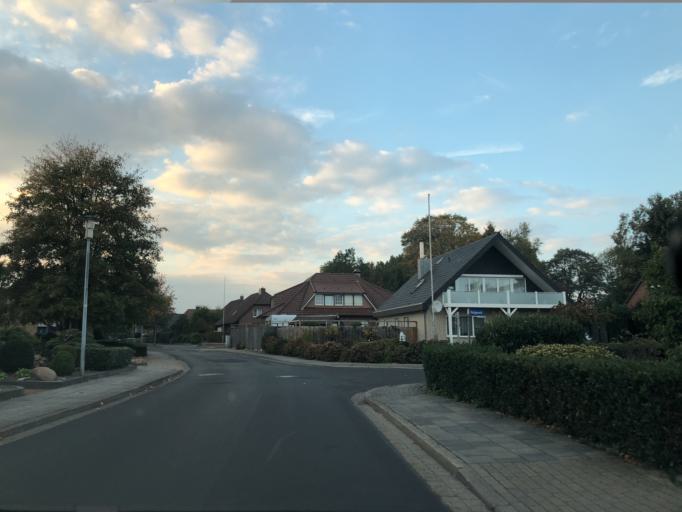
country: DE
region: Lower Saxony
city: Papenburg
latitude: 53.0775
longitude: 7.4368
